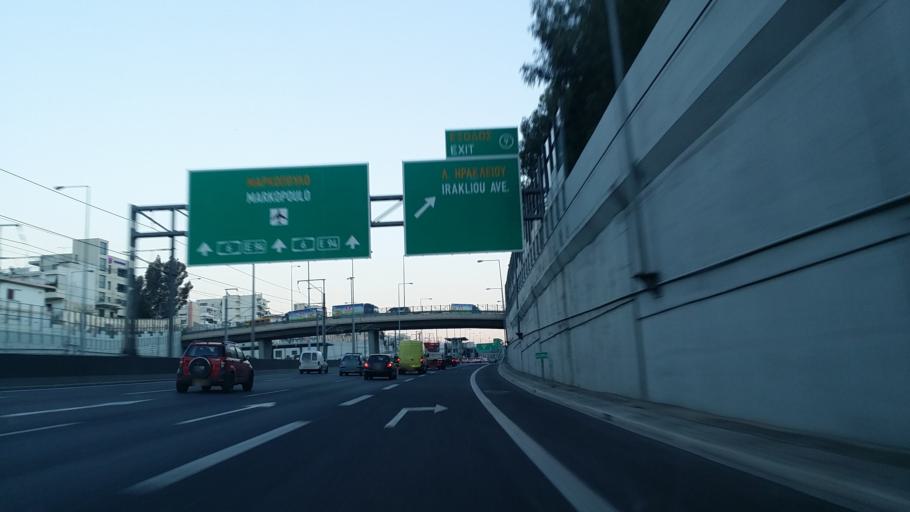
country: GR
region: Attica
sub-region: Nomarchia Athinas
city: Irakleio
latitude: 38.0590
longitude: 23.7661
